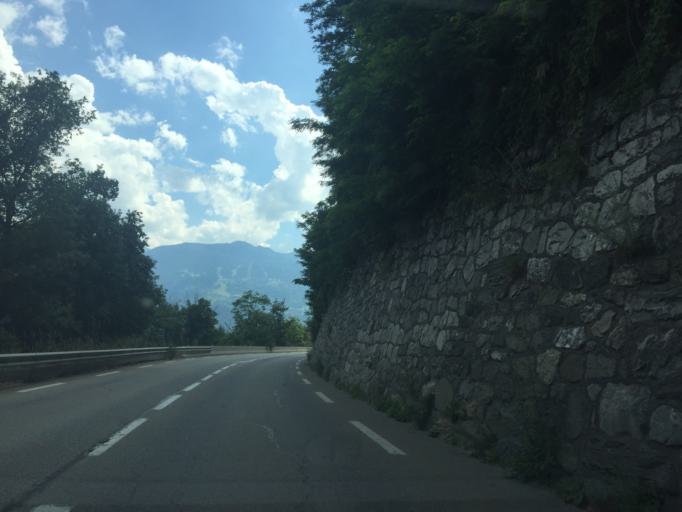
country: FR
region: Rhone-Alpes
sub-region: Departement de la Savoie
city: Bourg-Saint-Maurice
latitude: 45.6077
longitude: 6.7588
